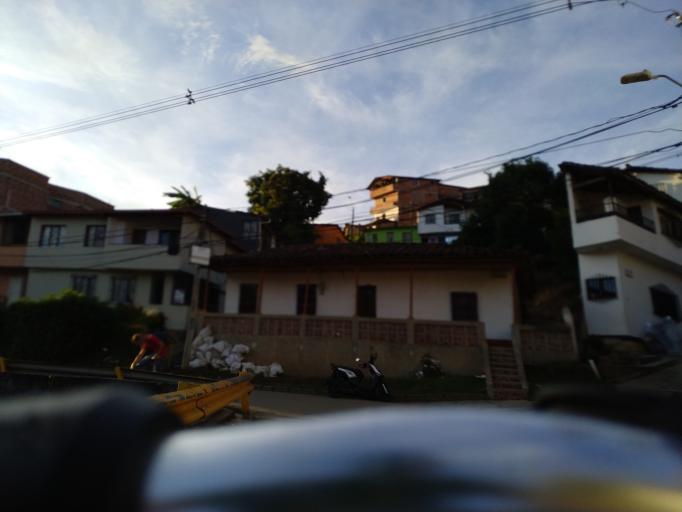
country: CO
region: Antioquia
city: Rionegro
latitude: 6.1589
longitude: -75.3764
